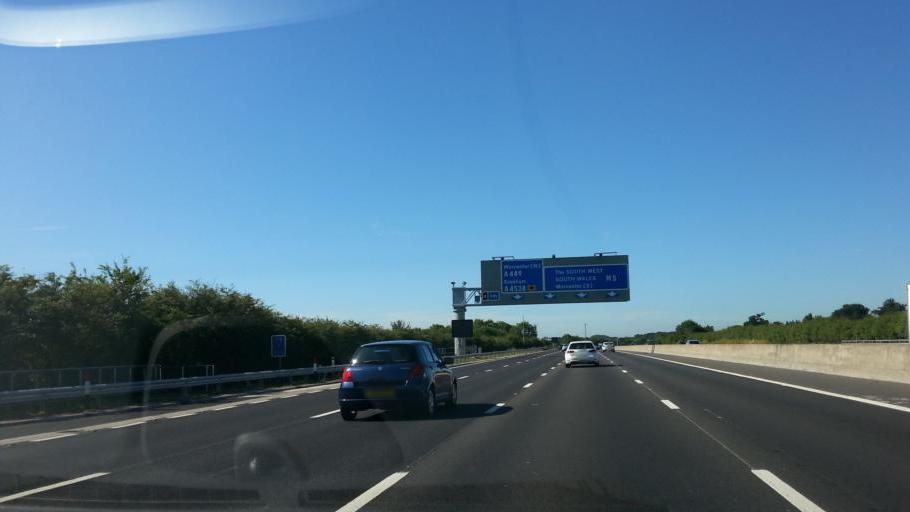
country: GB
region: England
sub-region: Worcestershire
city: Droitwich
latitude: 52.2316
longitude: -2.1396
